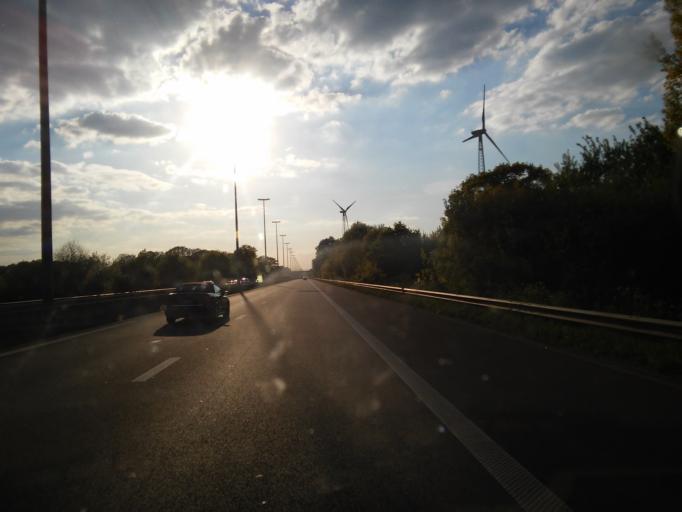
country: BE
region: Flanders
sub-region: Provincie Limburg
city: Tessenderlo
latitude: 51.0945
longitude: 5.0943
